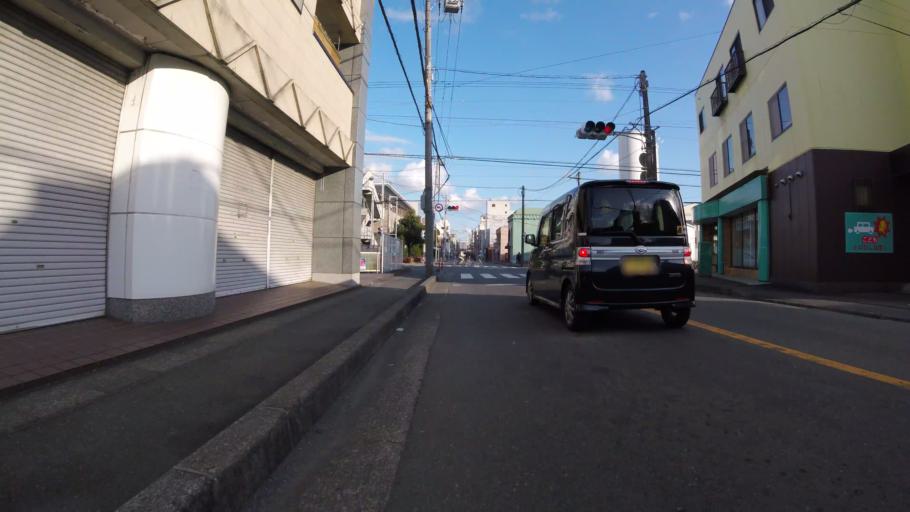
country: JP
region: Shizuoka
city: Fuji
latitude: 35.1541
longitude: 138.6478
